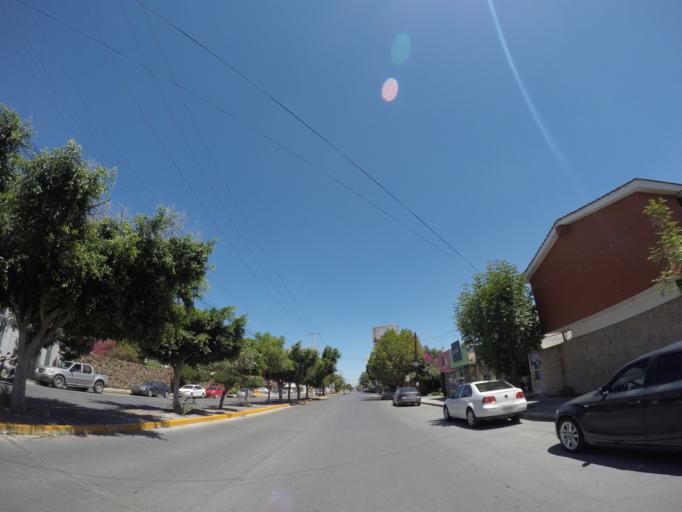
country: MX
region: San Luis Potosi
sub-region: San Luis Potosi
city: San Luis Potosi
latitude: 22.1468
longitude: -101.0106
